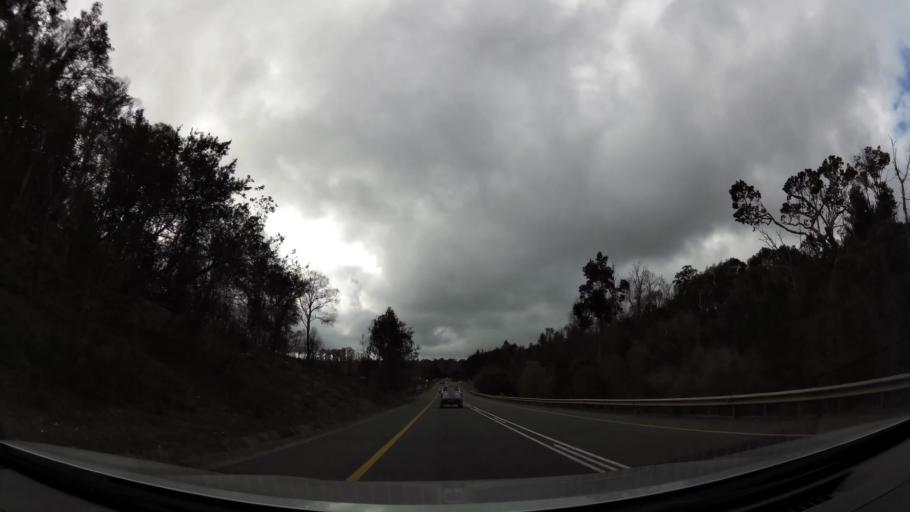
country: ZA
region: Western Cape
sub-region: Eden District Municipality
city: Knysna
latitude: -34.0322
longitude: 23.1587
